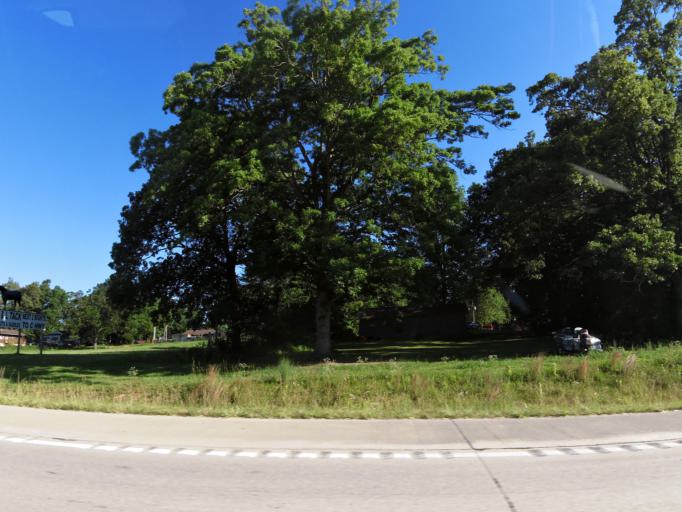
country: US
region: Missouri
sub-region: Butler County
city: Poplar Bluff
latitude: 36.6676
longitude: -90.5087
